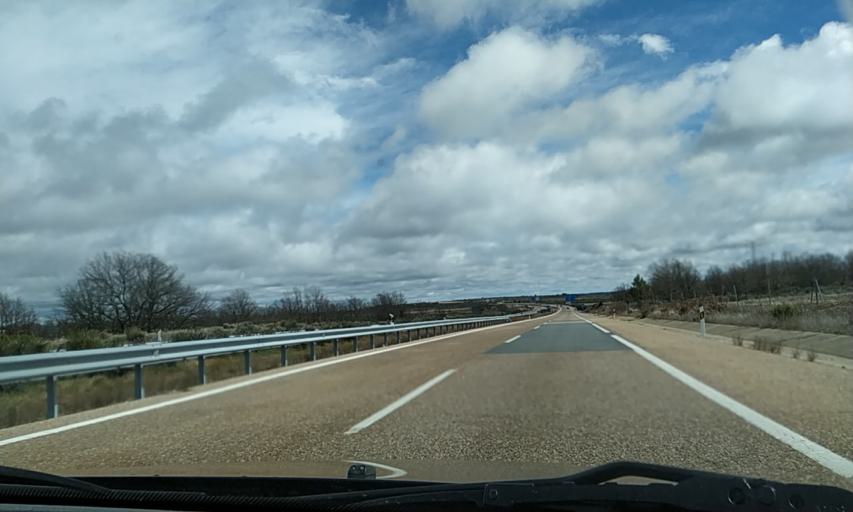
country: ES
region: Castille and Leon
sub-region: Provincia de Zamora
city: Mombuey
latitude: 42.0075
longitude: -6.2727
